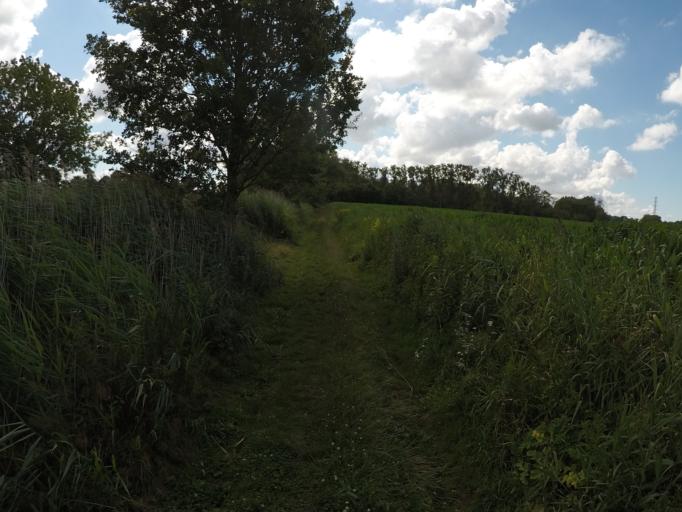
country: BE
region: Flanders
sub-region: Provincie Antwerpen
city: Stabroek
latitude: 51.3423
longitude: 4.3587
